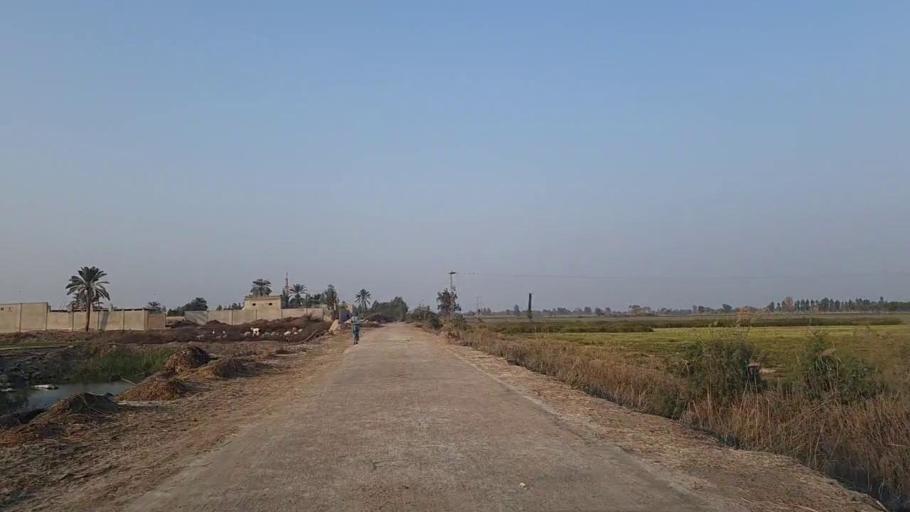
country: PK
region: Sindh
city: Daur
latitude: 26.4233
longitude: 68.3935
